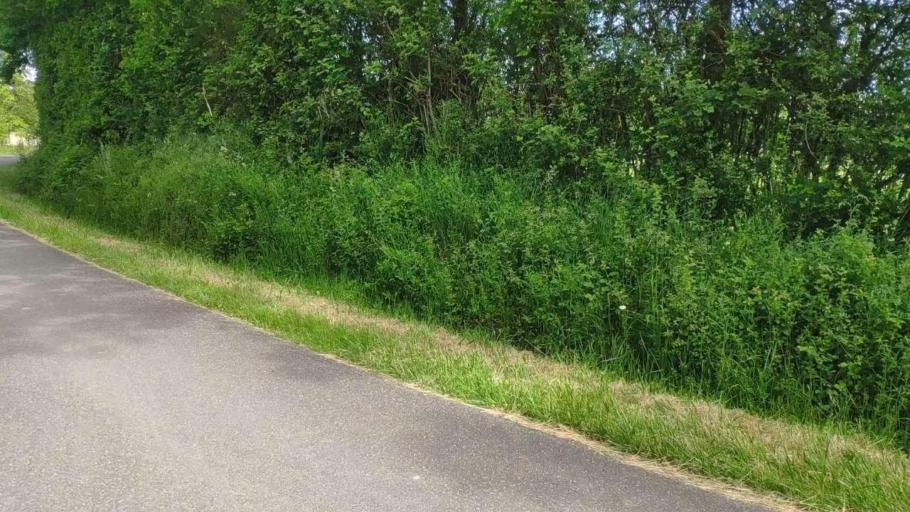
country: FR
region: Franche-Comte
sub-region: Departement du Jura
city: Bletterans
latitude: 46.6788
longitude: 5.4088
